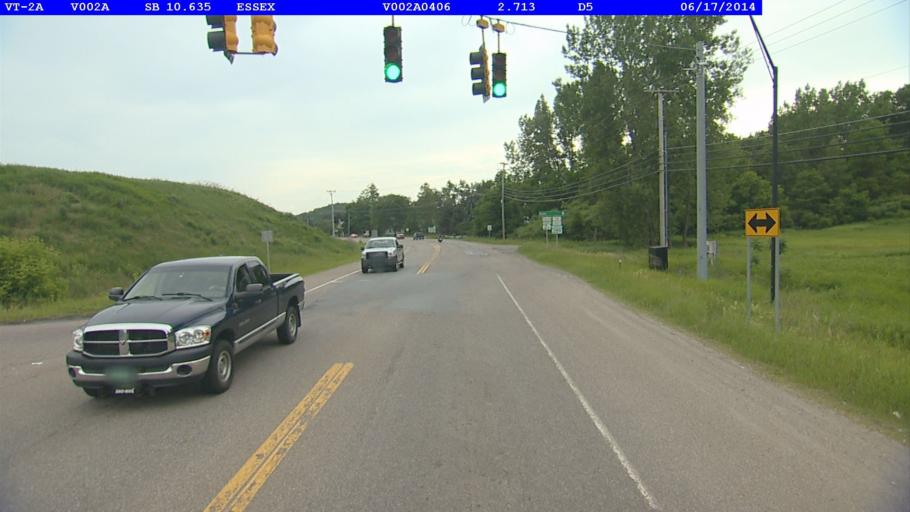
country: US
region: Vermont
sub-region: Chittenden County
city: Essex Junction
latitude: 44.5184
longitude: -73.1233
